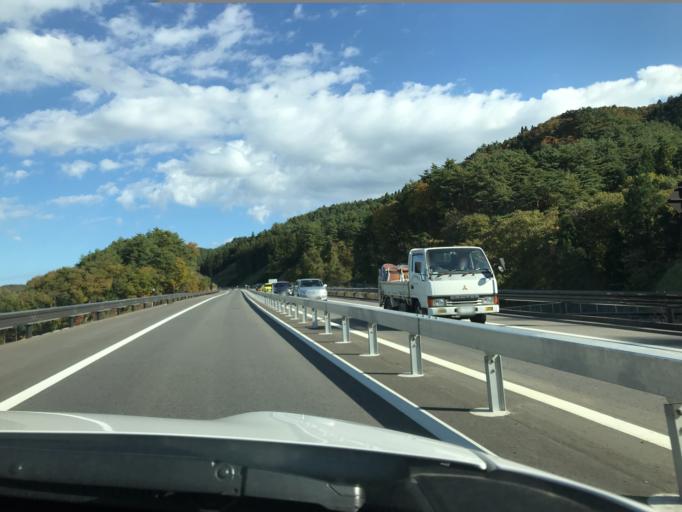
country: JP
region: Fukushima
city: Yanagawamachi-saiwaicho
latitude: 37.7547
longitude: 140.7056
